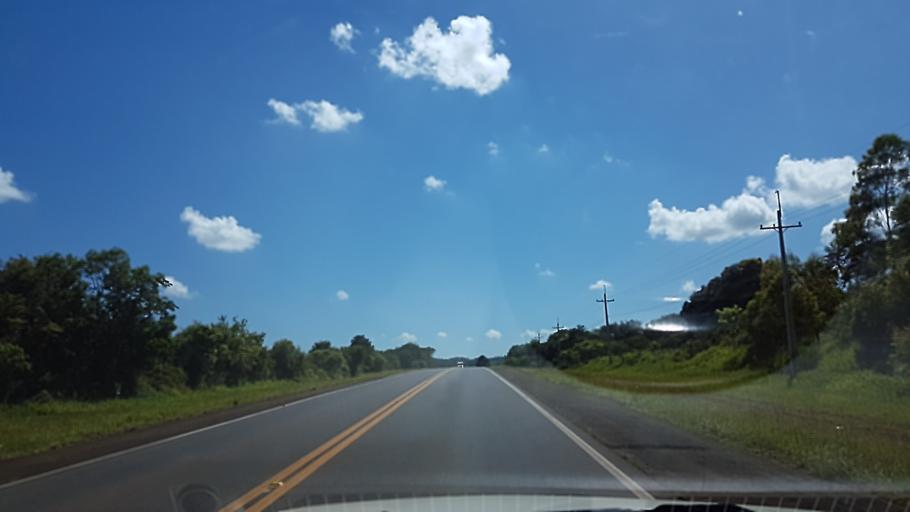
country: PY
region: Itapua
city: Carmen del Parana
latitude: -27.2169
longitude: -56.0943
